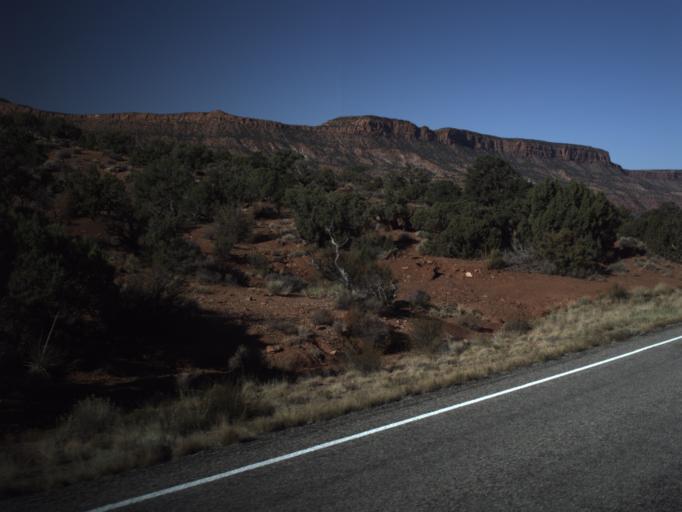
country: US
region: Utah
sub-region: San Juan County
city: Blanding
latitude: 37.6548
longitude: -110.1345
